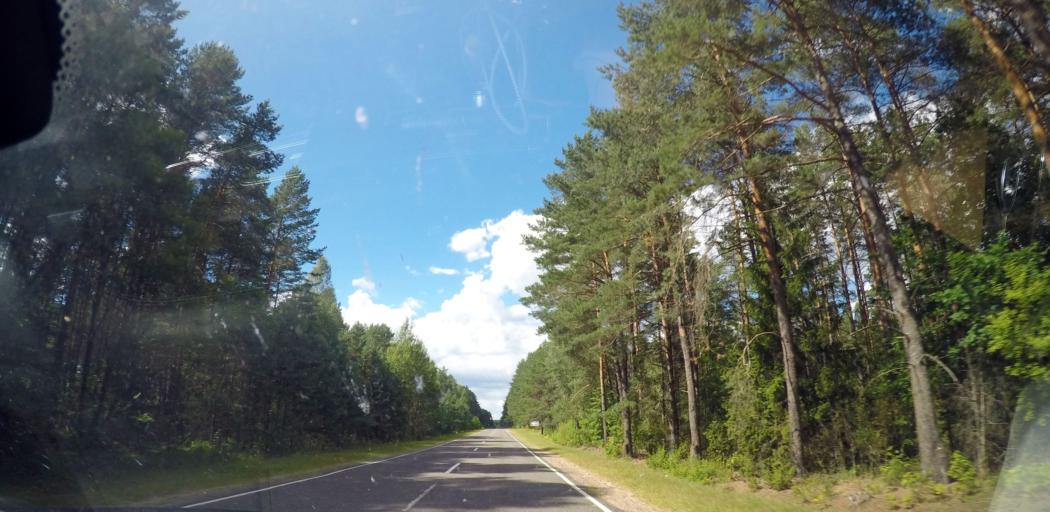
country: LT
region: Alytaus apskritis
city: Druskininkai
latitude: 53.8639
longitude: 24.1728
